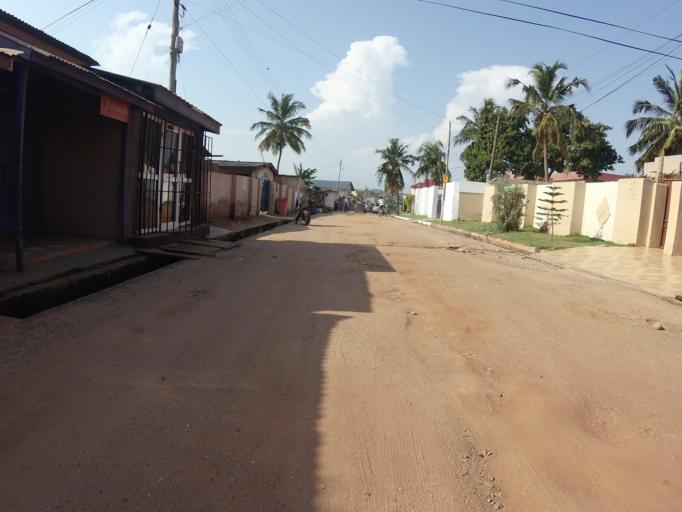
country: GH
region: Greater Accra
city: Dome
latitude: 5.6102
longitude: -0.2435
